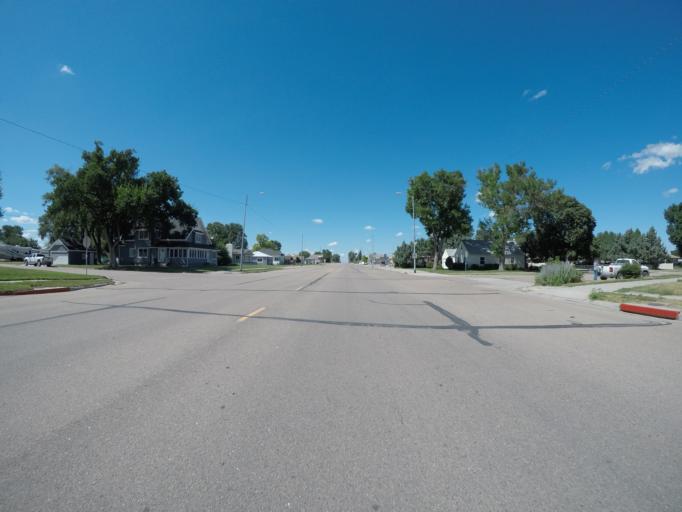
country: US
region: Nebraska
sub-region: Chase County
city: Imperial
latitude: 40.5219
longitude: -101.6431
